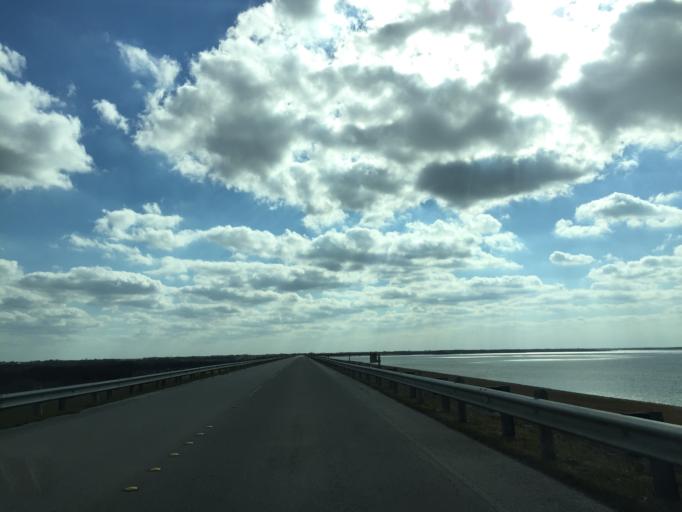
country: US
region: Texas
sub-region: Williamson County
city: Granger
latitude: 30.7105
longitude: -97.3255
